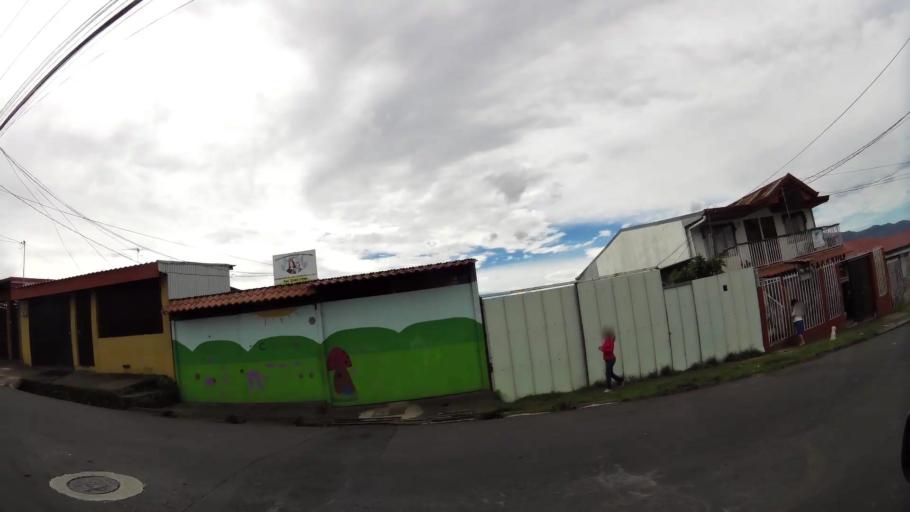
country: CR
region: San Jose
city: Purral
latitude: 9.9576
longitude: -84.0283
